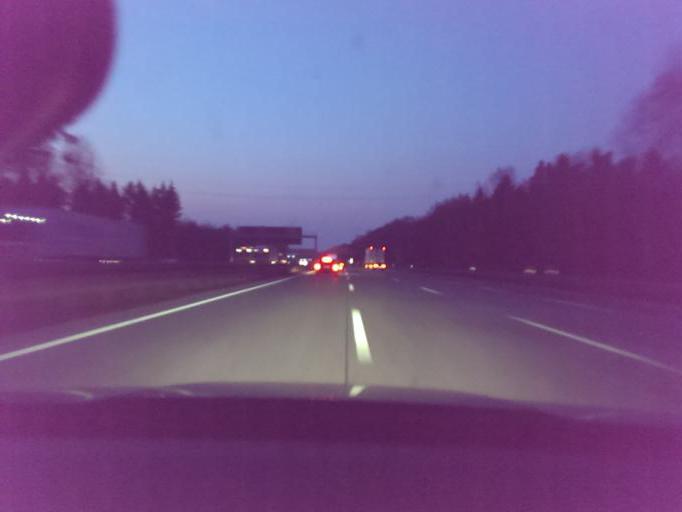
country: DE
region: Lower Saxony
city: Lehrte
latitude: 52.4039
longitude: 9.8989
